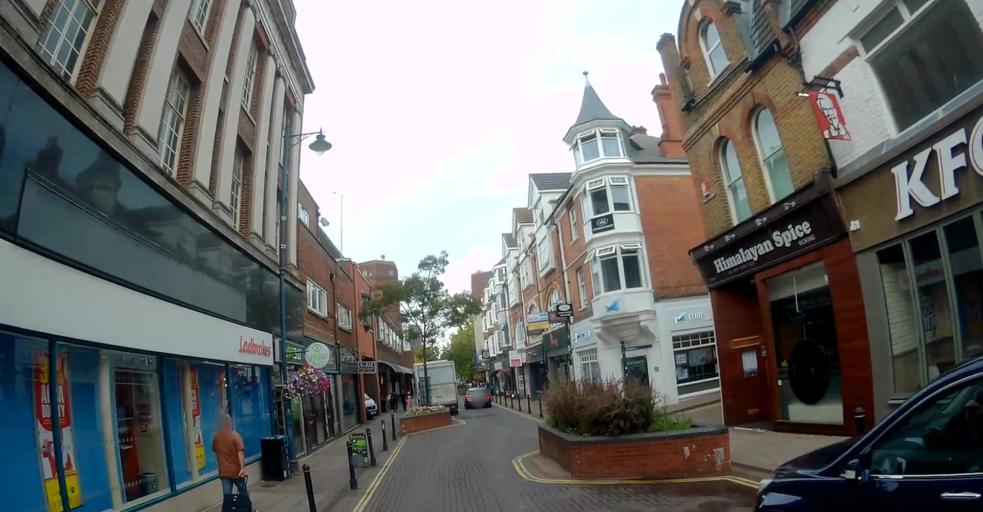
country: GB
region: England
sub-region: Surrey
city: Woking
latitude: 51.3199
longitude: -0.5561
